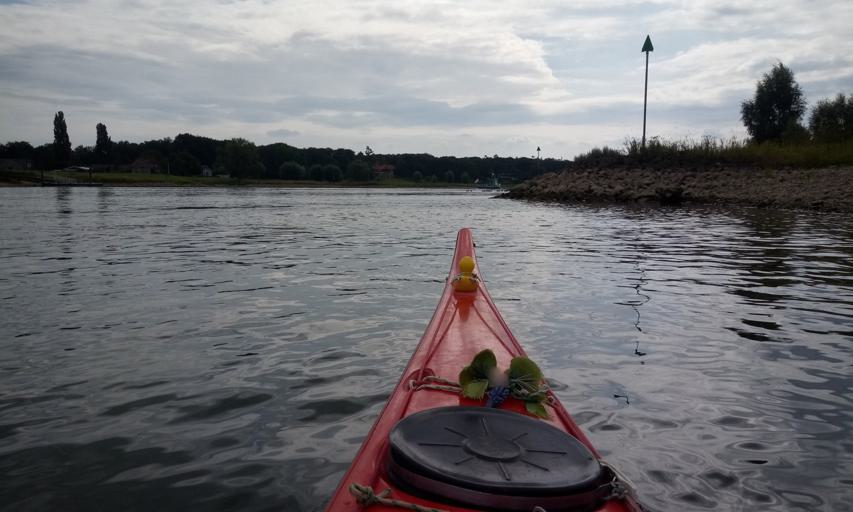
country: NL
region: Gelderland
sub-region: Gemeente Lochem
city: Gorssel
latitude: 52.2111
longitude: 6.1904
